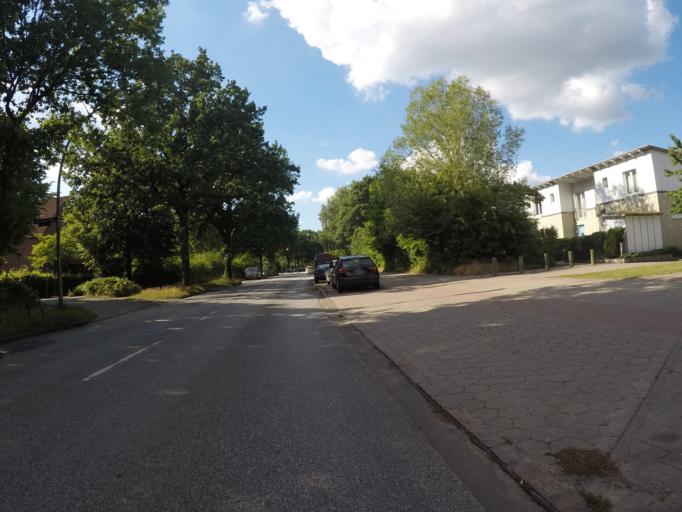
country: DE
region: Hamburg
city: Alsterdorf
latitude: 53.6138
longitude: 10.0086
